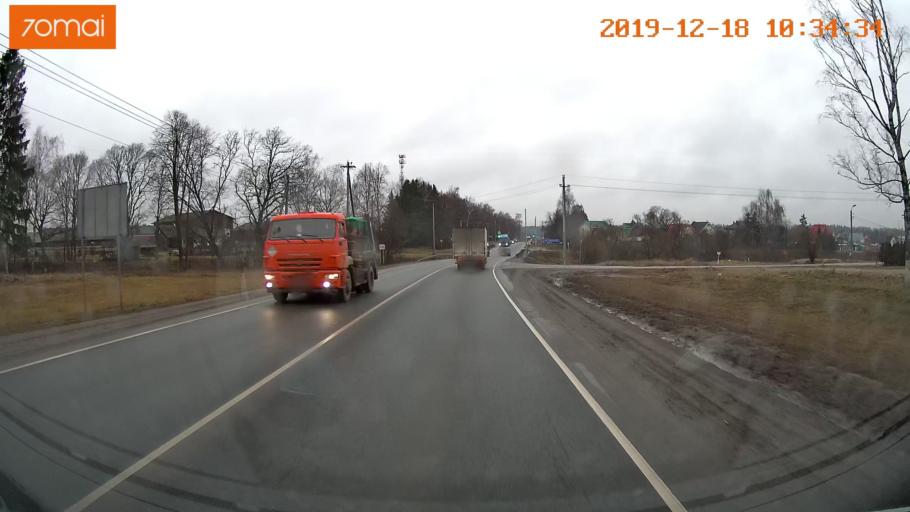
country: RU
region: Moskovskaya
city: Troitsk
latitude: 55.4077
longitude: 37.2022
